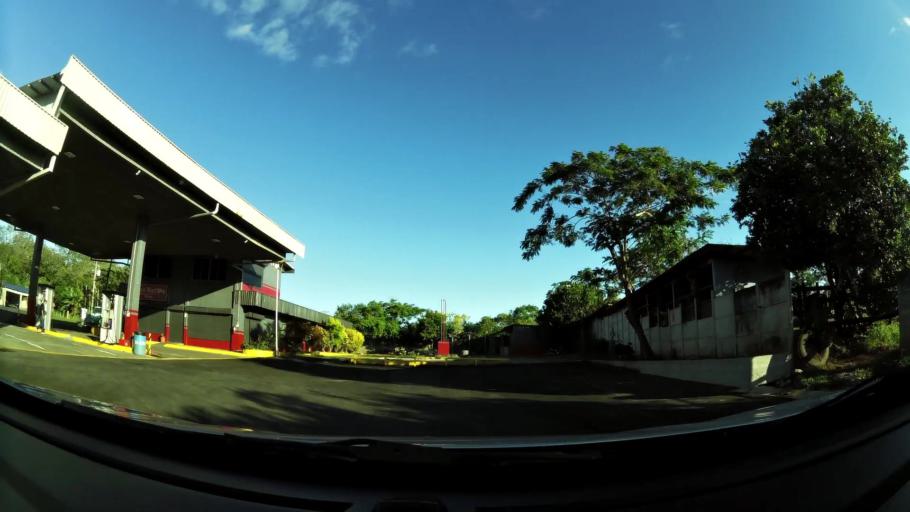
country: CR
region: Puntarenas
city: Miramar
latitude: 10.0948
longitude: -84.8203
